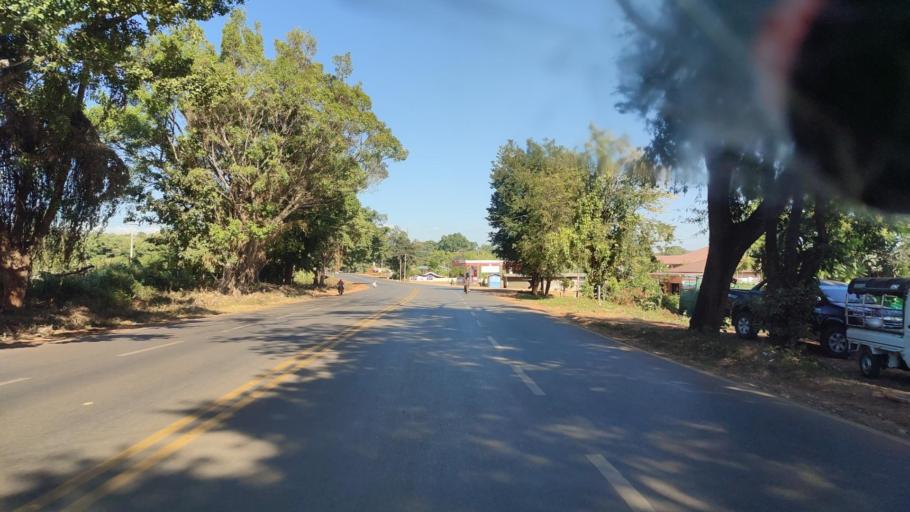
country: MM
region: Mandalay
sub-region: Pyin Oo Lwin District
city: Pyin Oo Lwin
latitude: 22.0899
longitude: 96.5856
